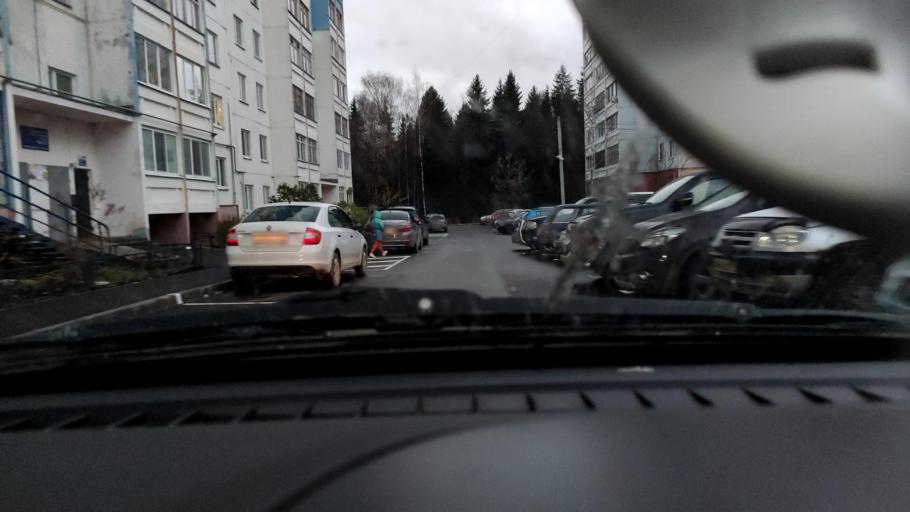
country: RU
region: Perm
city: Kondratovo
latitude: 58.0456
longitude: 56.0838
